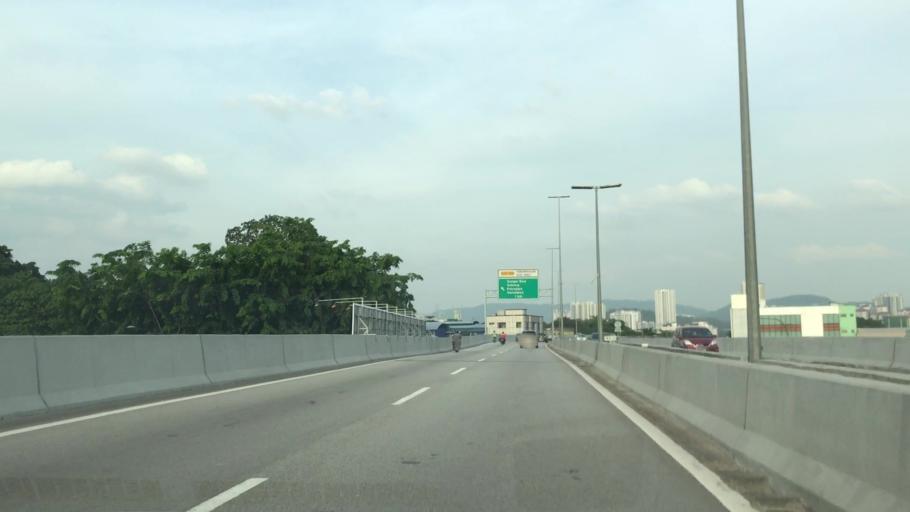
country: MY
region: Kuala Lumpur
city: Kuala Lumpur
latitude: 3.1221
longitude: 101.7083
